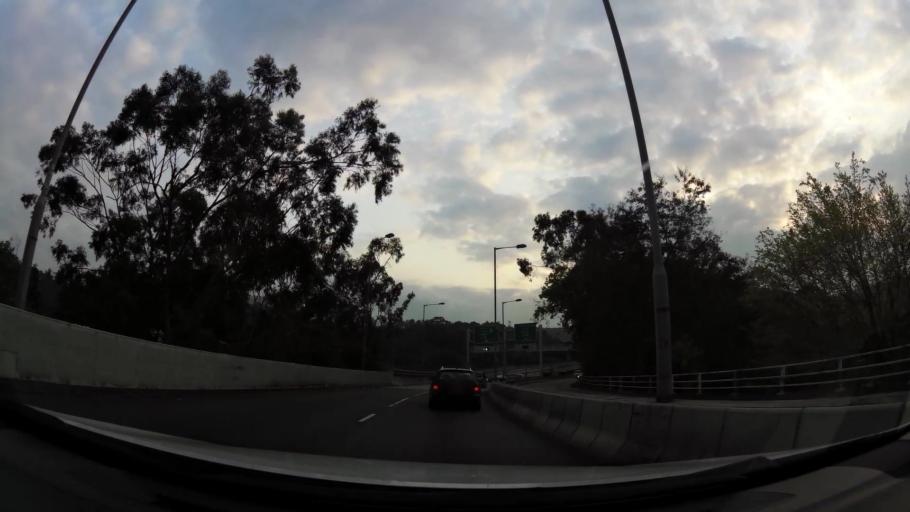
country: HK
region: Tai Po
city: Tai Po
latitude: 22.4503
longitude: 114.1577
